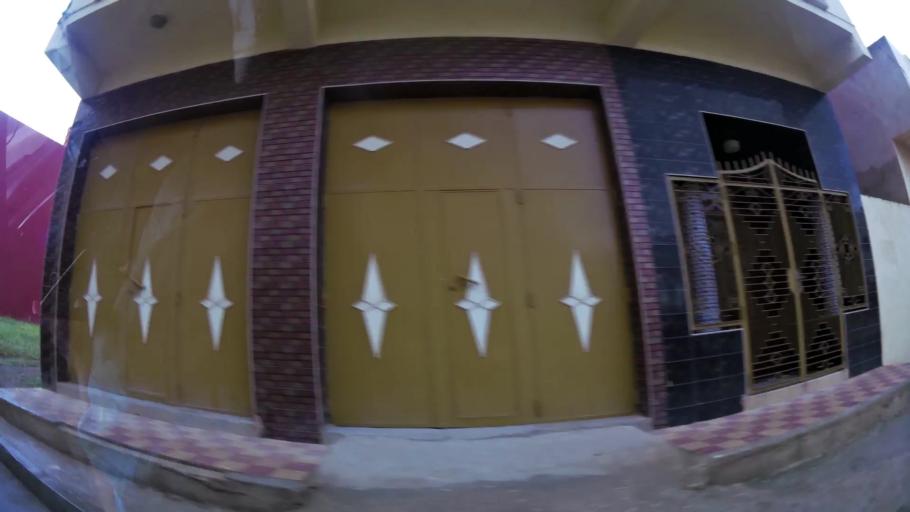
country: MA
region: Oriental
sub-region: Nador
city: Nador
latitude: 35.1494
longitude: -2.9980
